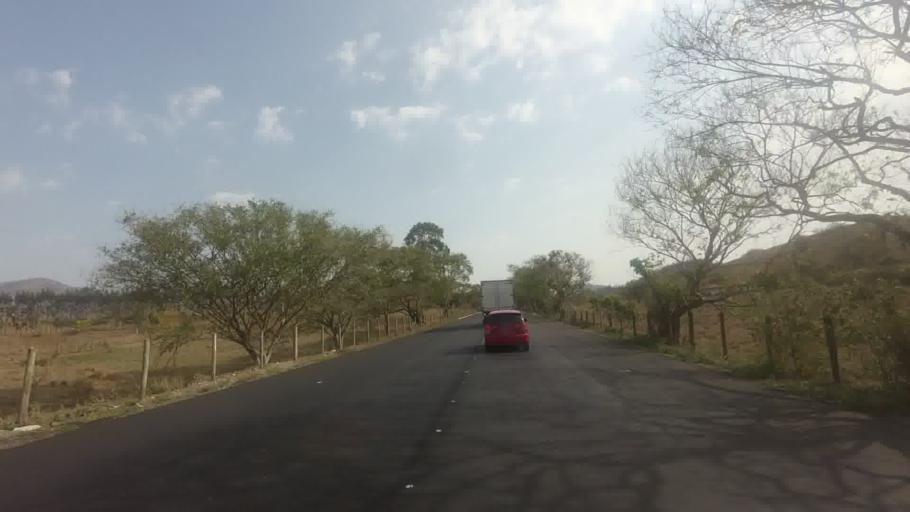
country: BR
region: Rio de Janeiro
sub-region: Bom Jesus Do Itabapoana
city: Bom Jesus do Itabapoana
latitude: -21.1799
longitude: -41.6862
